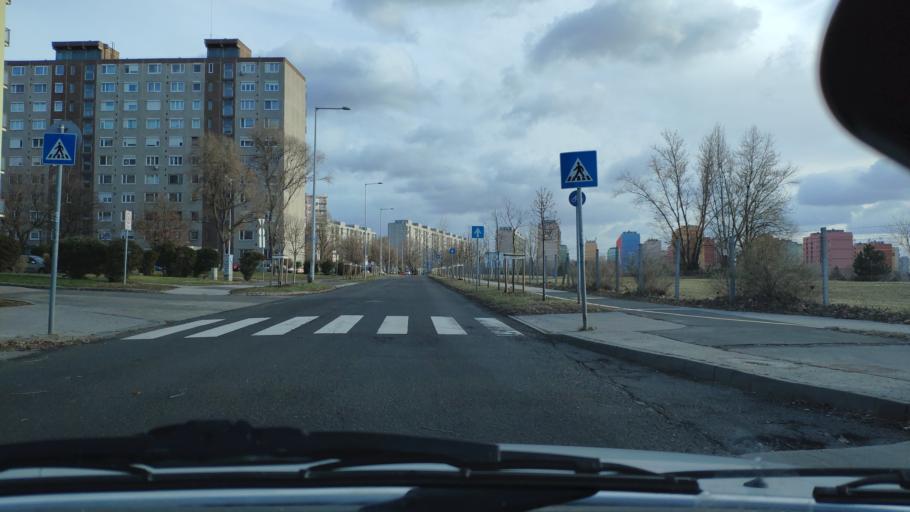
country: HU
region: Budapest
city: Budapest X. keruelet
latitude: 47.4753
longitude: 19.1572
